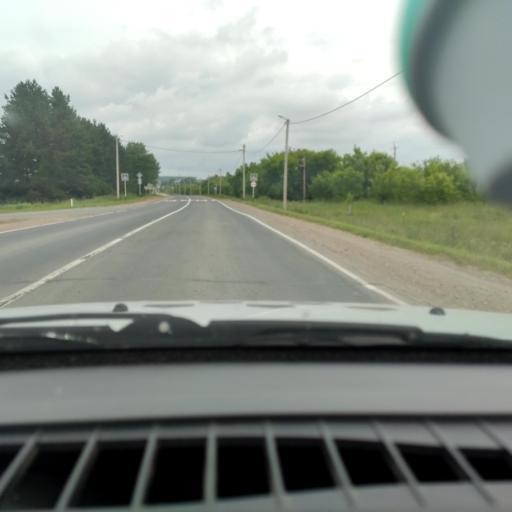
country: RU
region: Perm
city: Ust'-Kishert'
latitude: 57.5955
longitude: 57.3248
